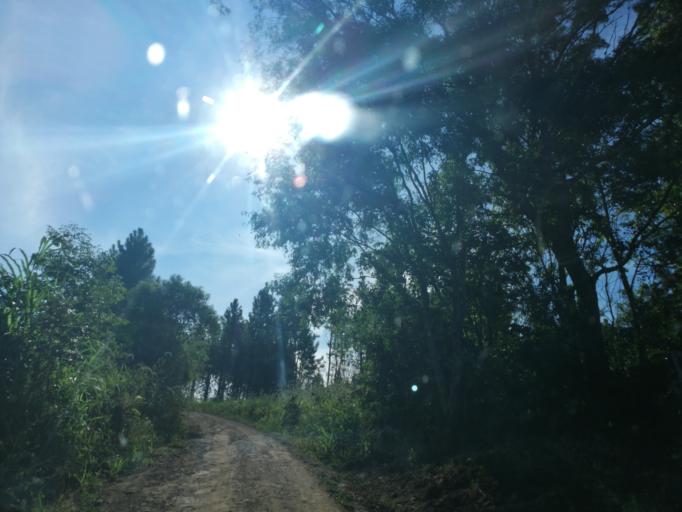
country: AR
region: Misiones
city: Dos de Mayo
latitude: -27.0163
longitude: -54.4232
